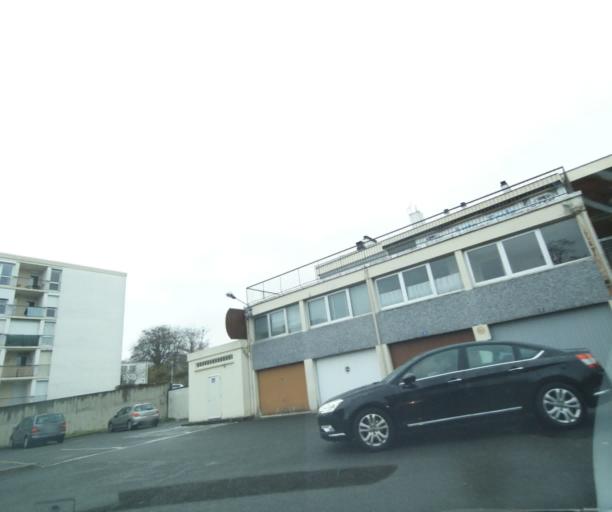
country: FR
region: Ile-de-France
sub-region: Departement de Seine-et-Marne
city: Avon
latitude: 48.4132
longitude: 2.7363
